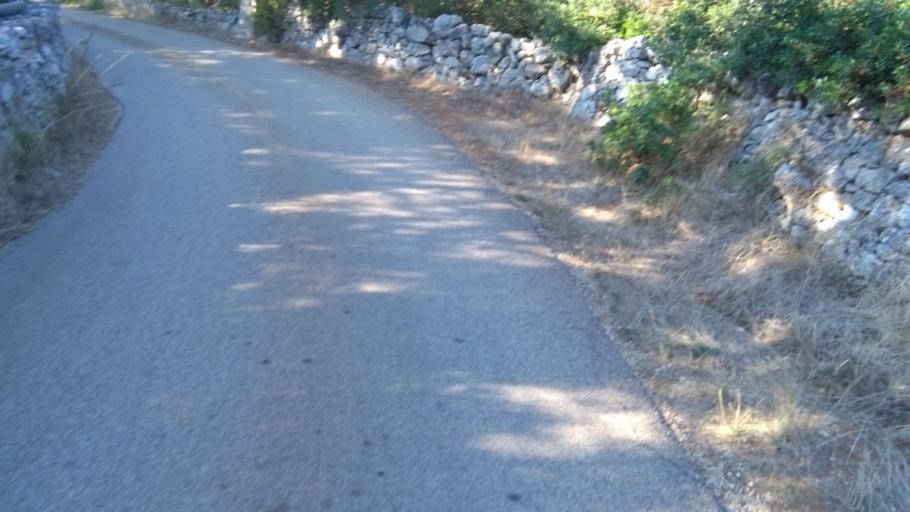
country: IT
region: Apulia
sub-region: Provincia di Bari
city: Putignano
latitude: 40.8268
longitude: 17.0590
